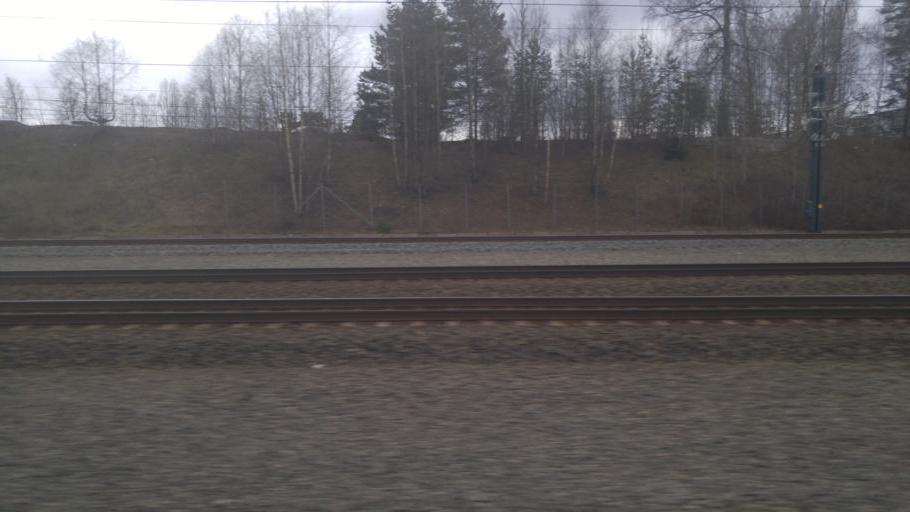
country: NO
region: Akershus
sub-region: Nannestad
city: Teigebyen
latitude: 60.1900
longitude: 11.0953
